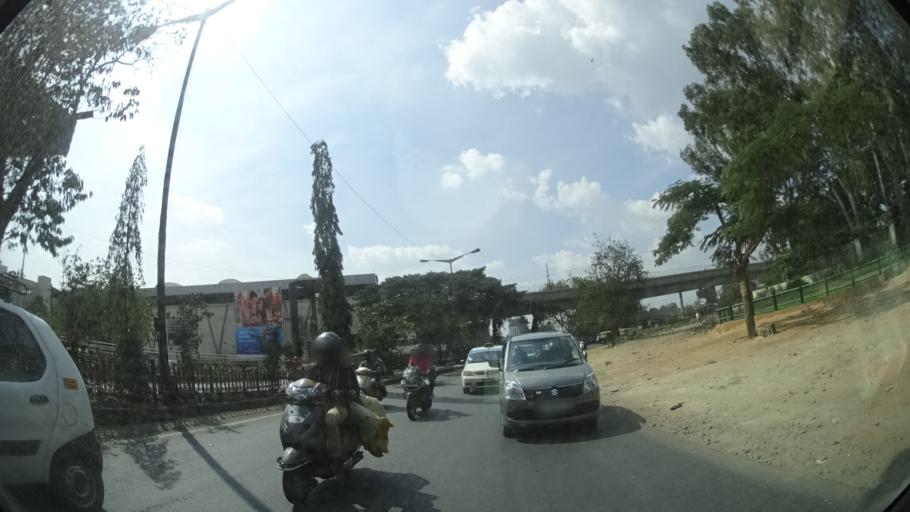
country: IN
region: Karnataka
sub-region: Bangalore Urban
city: Bangalore
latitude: 13.0158
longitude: 77.5544
